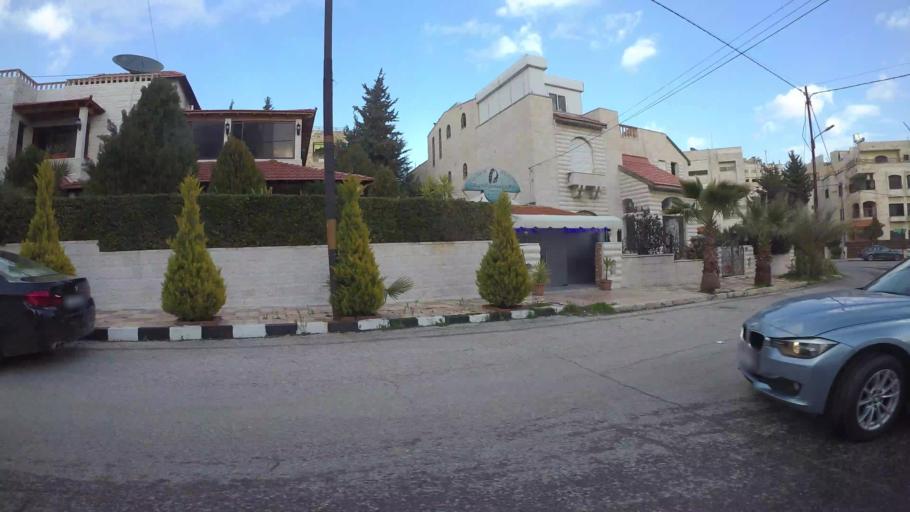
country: JO
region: Amman
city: Al Jubayhah
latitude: 31.9806
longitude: 35.8635
